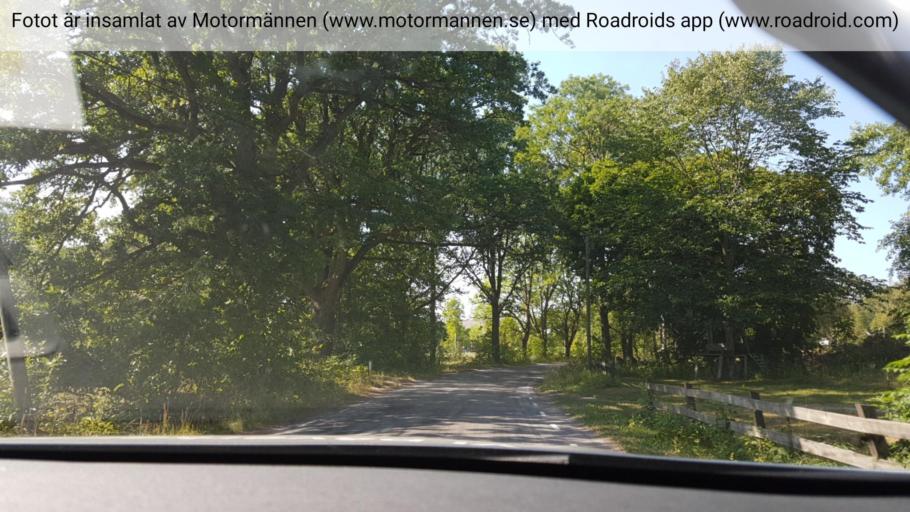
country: SE
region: Vaestra Goetaland
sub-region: Mariestads Kommun
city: Mariestad
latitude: 58.6121
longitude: 13.8786
